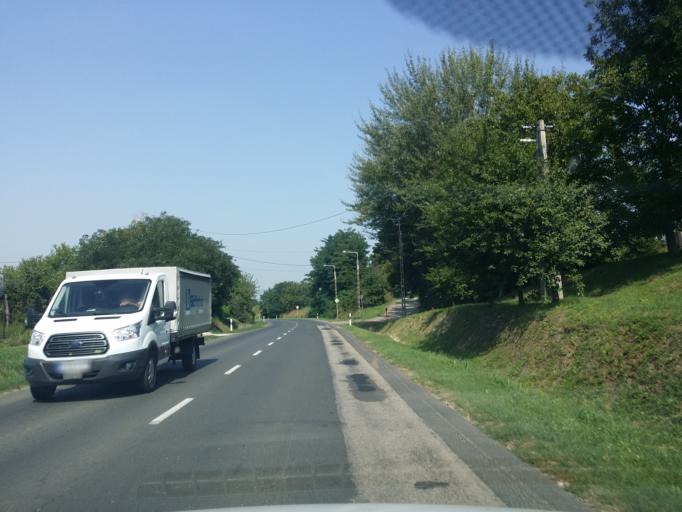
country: HU
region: Tolna
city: Pincehely
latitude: 46.7212
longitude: 18.4868
